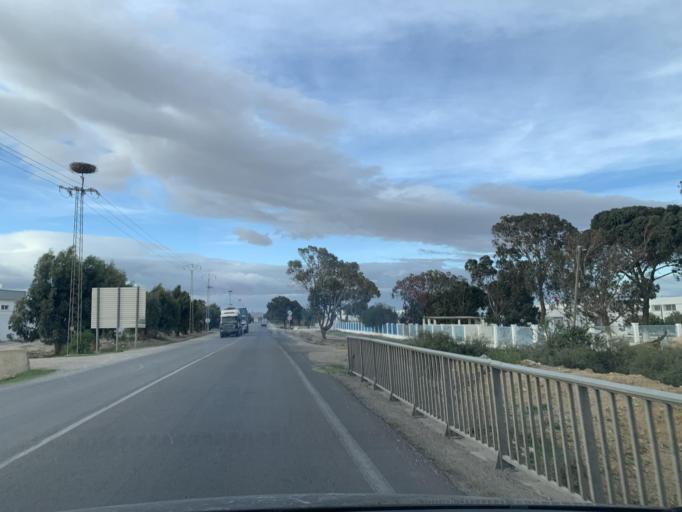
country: TN
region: Susah
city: Harqalah
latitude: 36.1043
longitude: 10.3877
